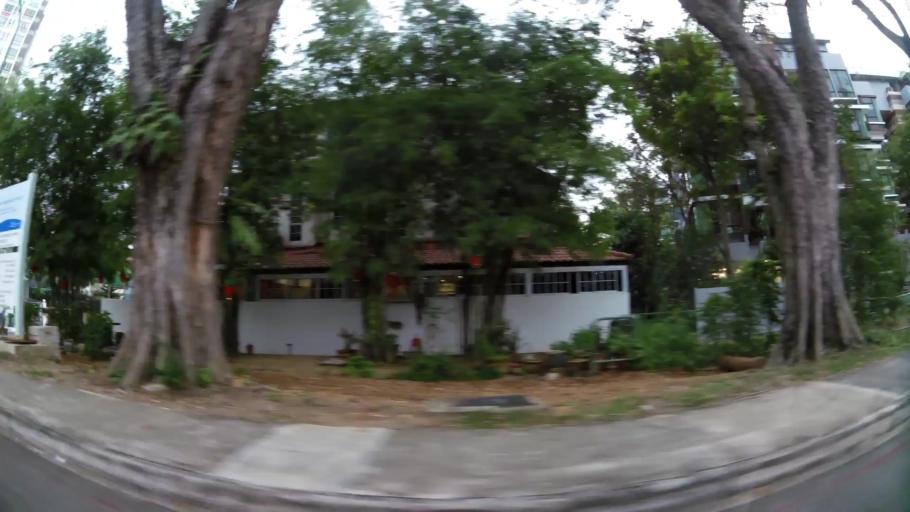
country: SG
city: Singapore
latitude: 1.3138
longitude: 103.8926
